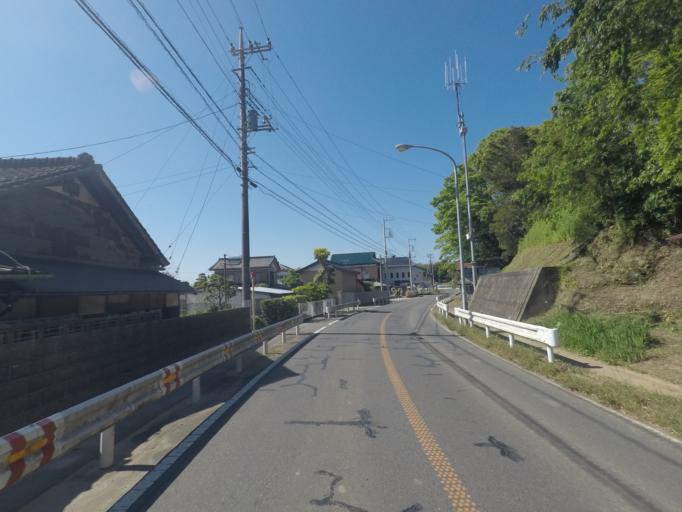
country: JP
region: Ibaraki
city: Inashiki
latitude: 36.0711
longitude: 140.4291
